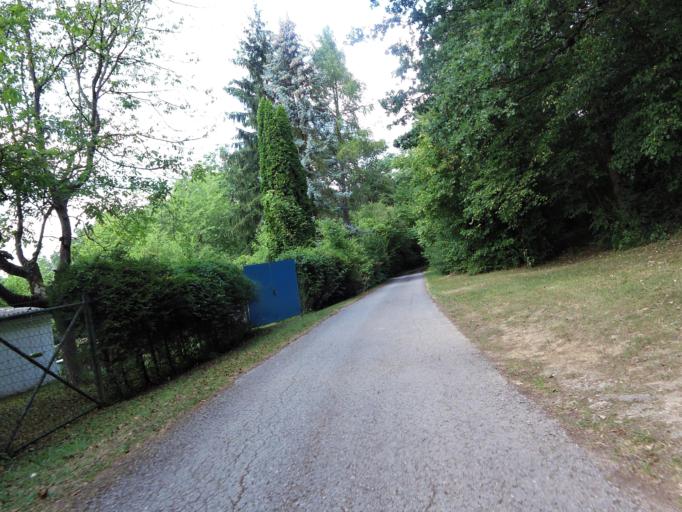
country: DE
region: Bavaria
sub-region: Regierungsbezirk Unterfranken
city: Gerbrunn
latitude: 49.7808
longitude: 9.9999
